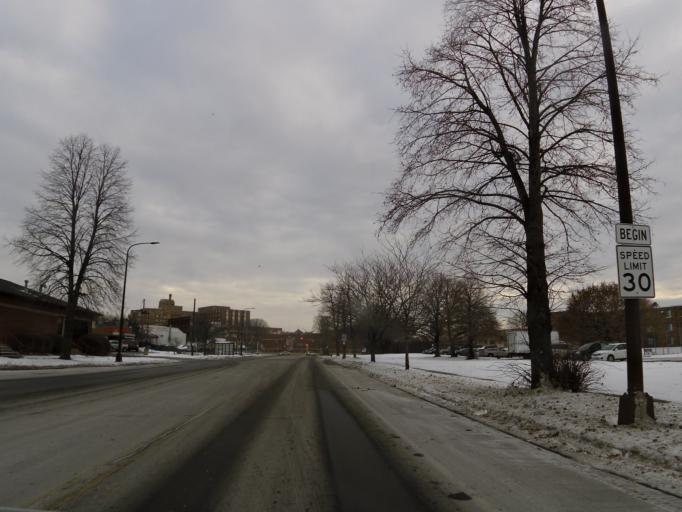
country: US
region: Minnesota
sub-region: Ramsey County
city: Saint Paul
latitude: 44.9599
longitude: -93.1079
